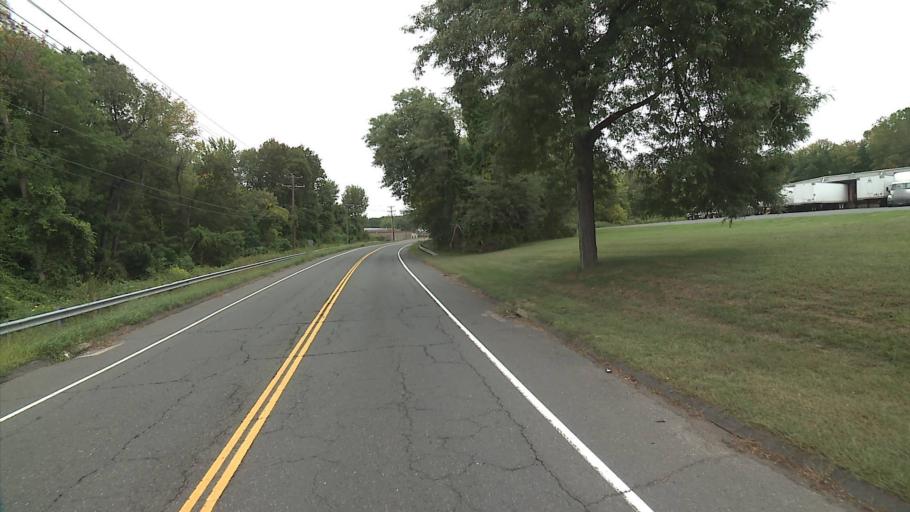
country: US
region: Connecticut
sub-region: Hartford County
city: Windsor Locks
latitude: 41.9412
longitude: -72.6112
